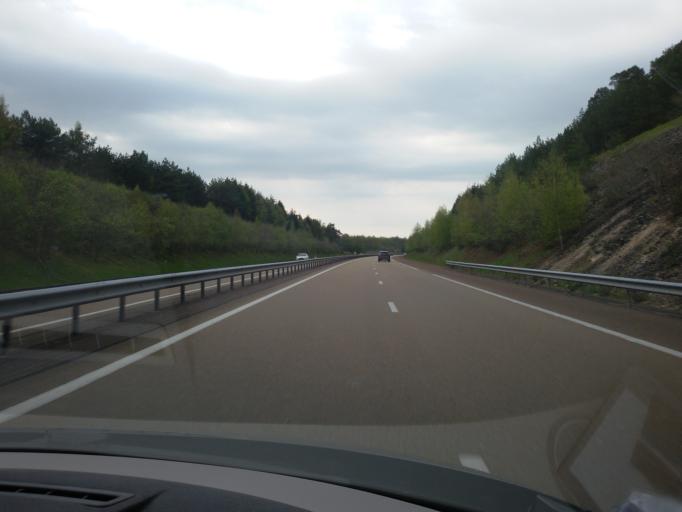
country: FR
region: Champagne-Ardenne
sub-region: Departement de la Haute-Marne
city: Chamarandes-Choignes
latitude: 48.0093
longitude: 5.1050
